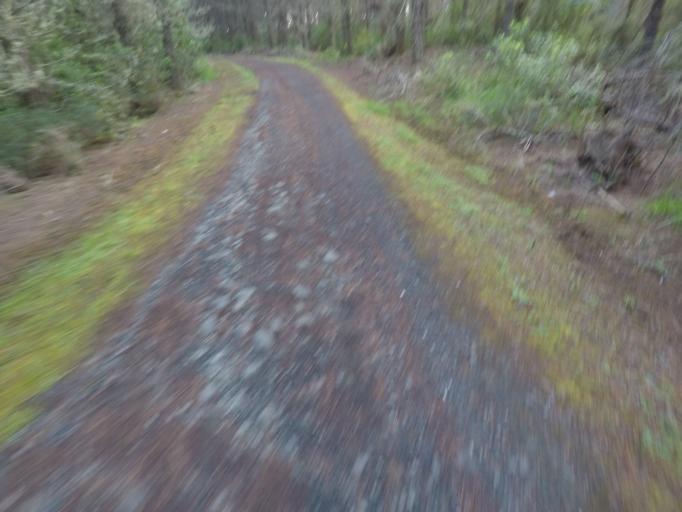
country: NZ
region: Auckland
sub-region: Auckland
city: Parakai
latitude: -36.7094
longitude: 174.5786
